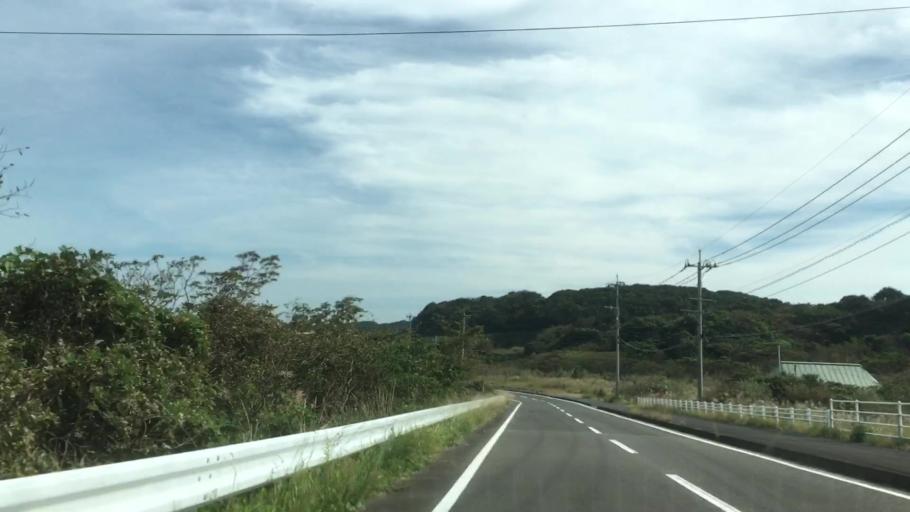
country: JP
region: Nagasaki
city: Sasebo
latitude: 33.0119
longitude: 129.5700
